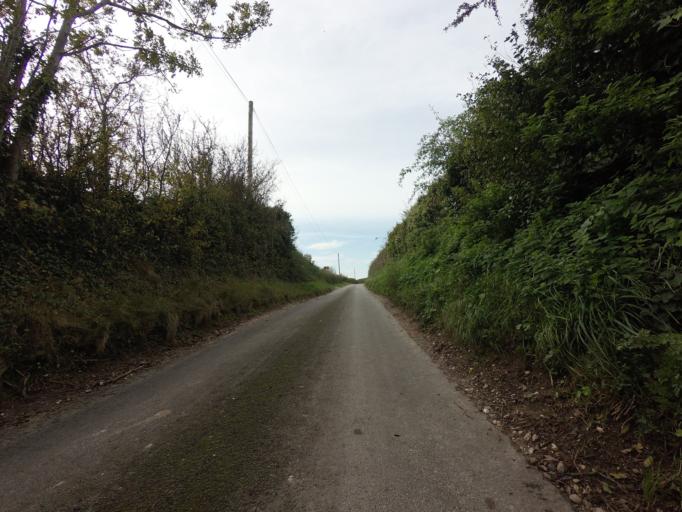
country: GB
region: England
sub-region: Norfolk
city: Wells-next-the-Sea
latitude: 52.9411
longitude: 0.7071
